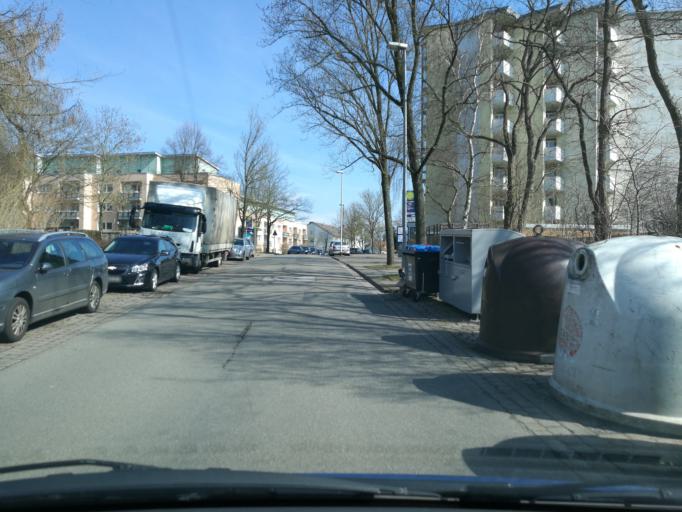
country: DE
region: Lower Saxony
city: Ronnenberg
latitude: 52.3717
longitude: 9.6618
